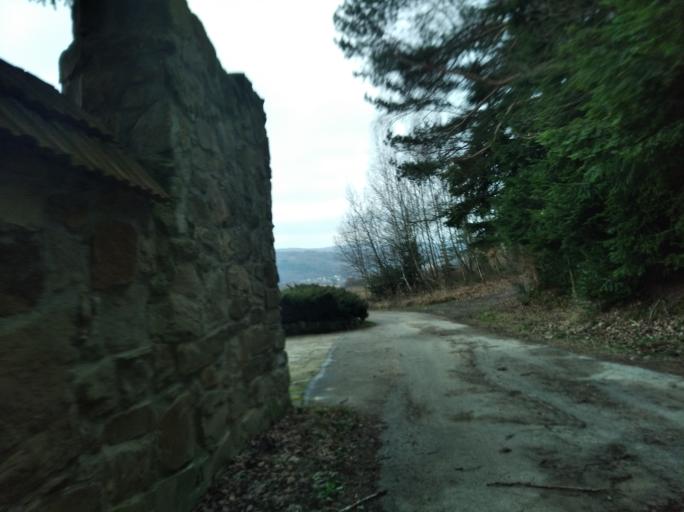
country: PL
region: Subcarpathian Voivodeship
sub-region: Powiat strzyzowski
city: Strzyzow
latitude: 49.9033
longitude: 21.8131
